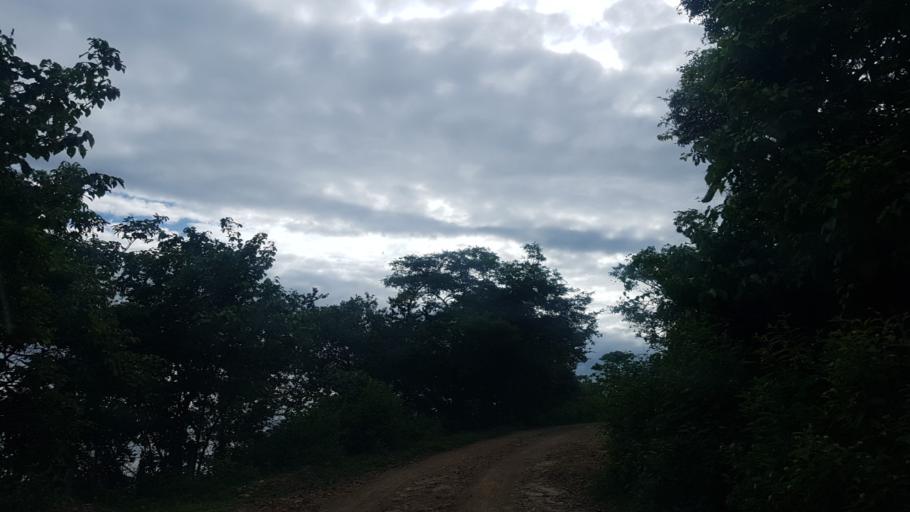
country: NI
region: Nueva Segovia
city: Mozonte
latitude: 13.5922
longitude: -86.4142
